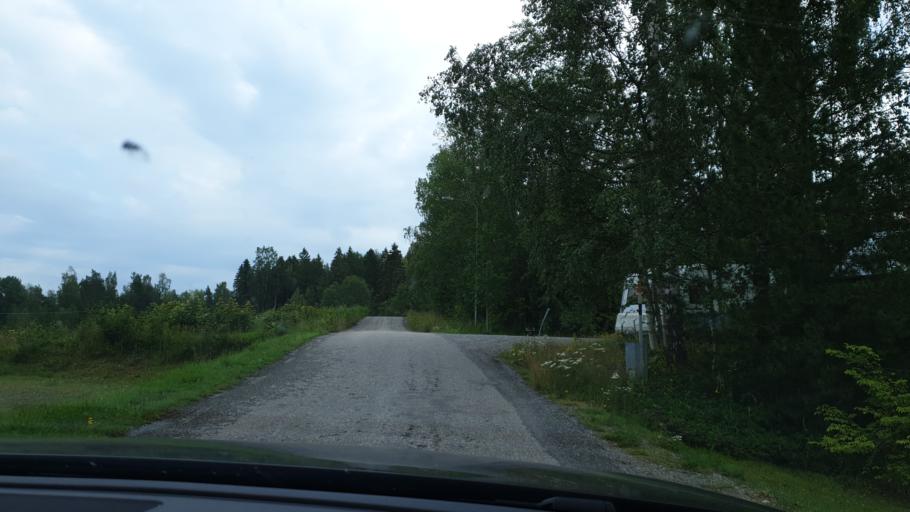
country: SE
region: Gaevleborg
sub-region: Hudiksvalls Kommun
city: Iggesund
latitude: 61.5407
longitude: 17.0062
